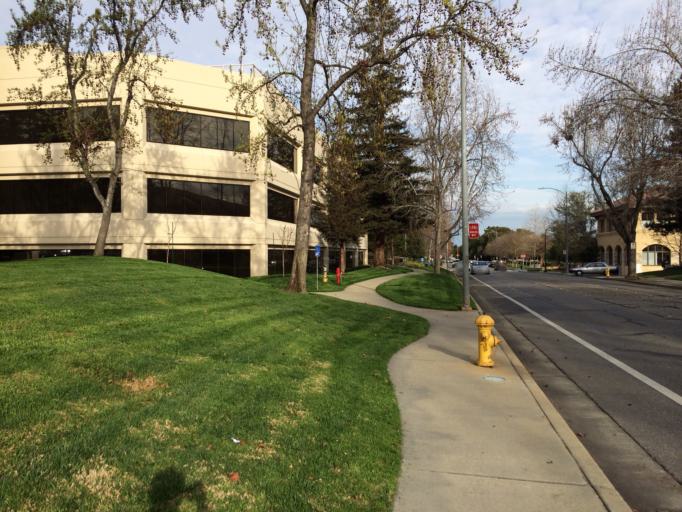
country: US
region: California
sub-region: Santa Clara County
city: Cupertino
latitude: 37.3193
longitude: -122.0307
